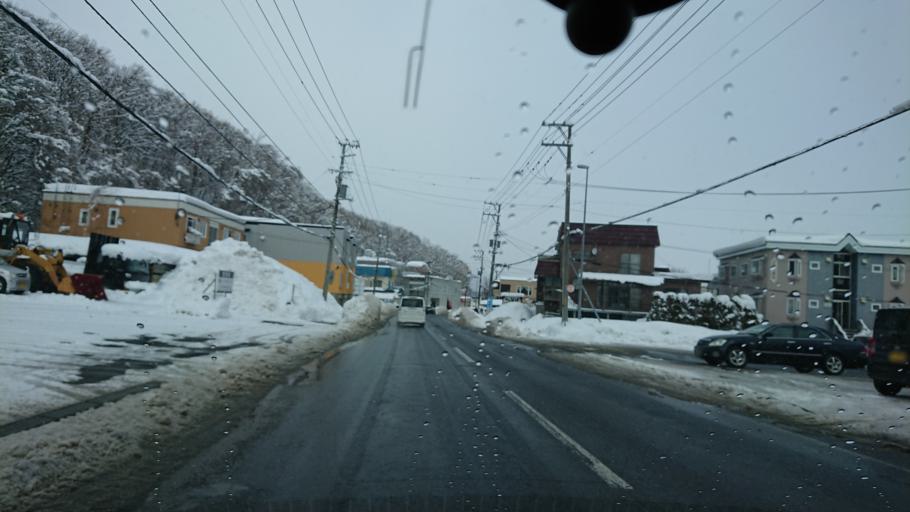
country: JP
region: Hokkaido
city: Sapporo
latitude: 42.9652
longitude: 141.3429
